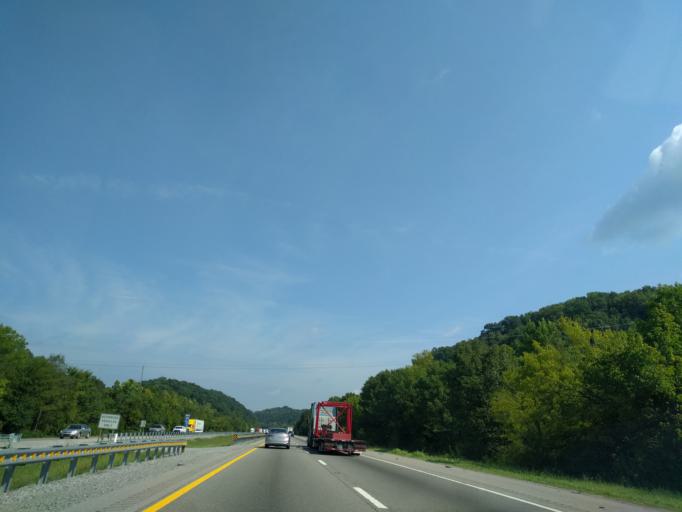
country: US
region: Tennessee
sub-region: Sumner County
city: Millersville
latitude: 36.3879
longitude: -86.7151
